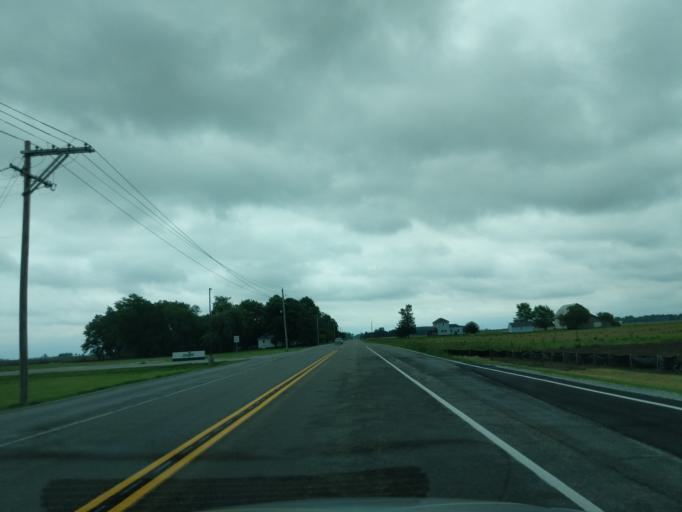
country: US
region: Indiana
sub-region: Tipton County
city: Tipton
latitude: 40.2834
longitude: -86.0044
